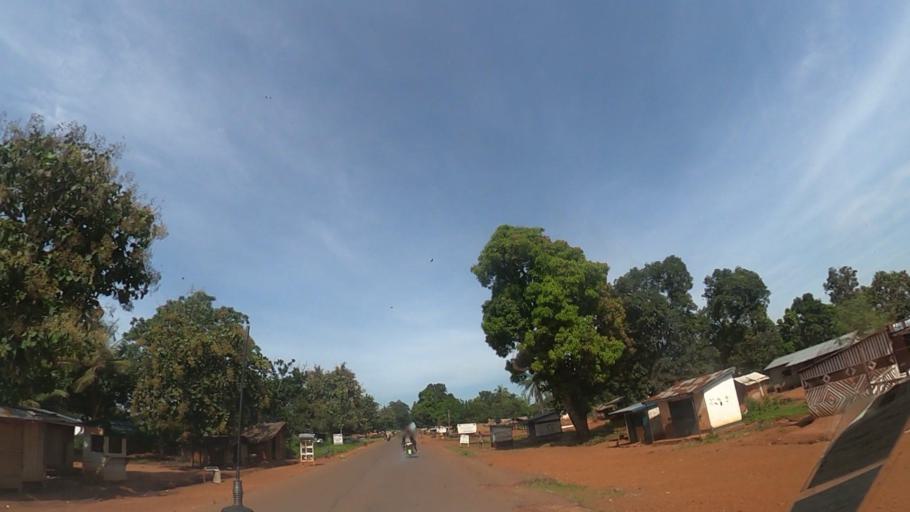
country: CF
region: Ombella-Mpoko
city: Bimbo
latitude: 4.3118
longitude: 18.4797
